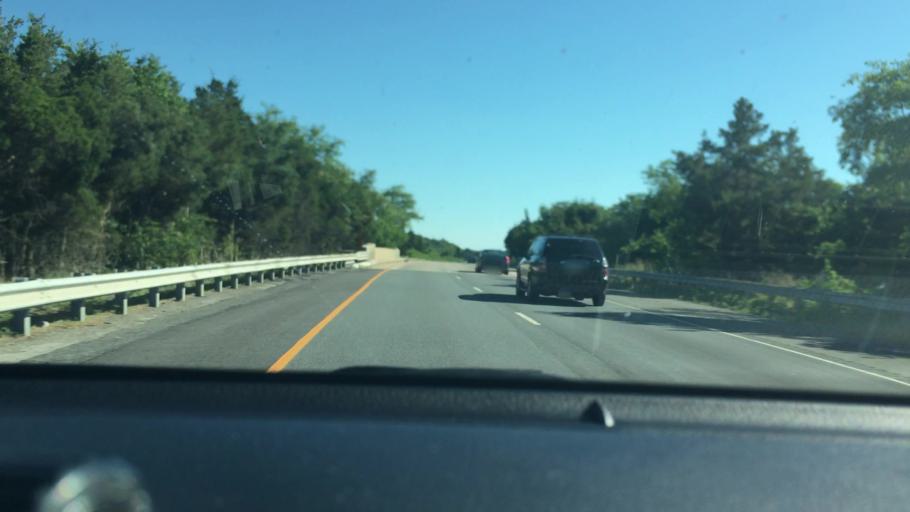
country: US
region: New Jersey
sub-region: Gloucester County
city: Newfield
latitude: 39.5482
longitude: -75.0589
